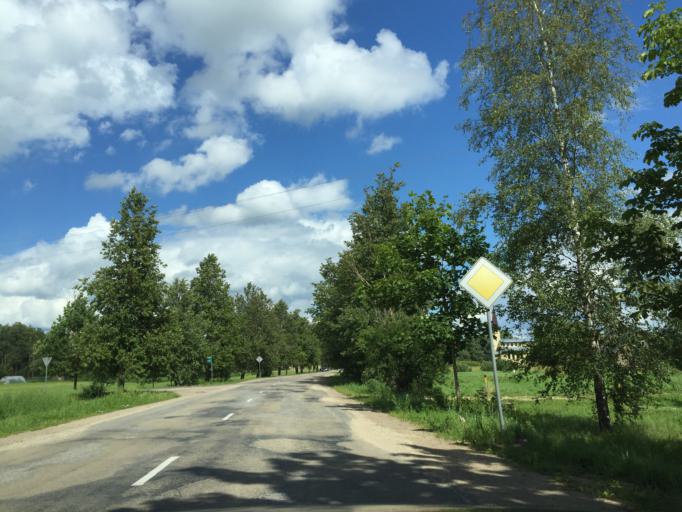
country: LV
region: Malpils
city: Malpils
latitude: 56.9016
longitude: 24.9227
